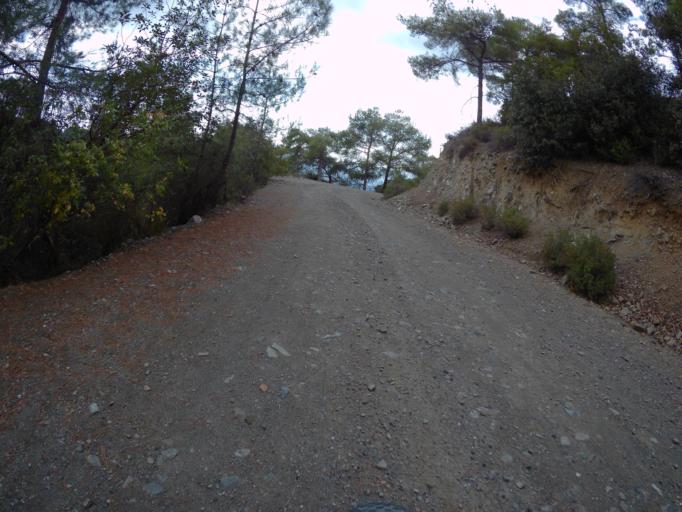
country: CY
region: Lefkosia
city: Kakopetria
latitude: 34.8996
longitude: 32.8466
